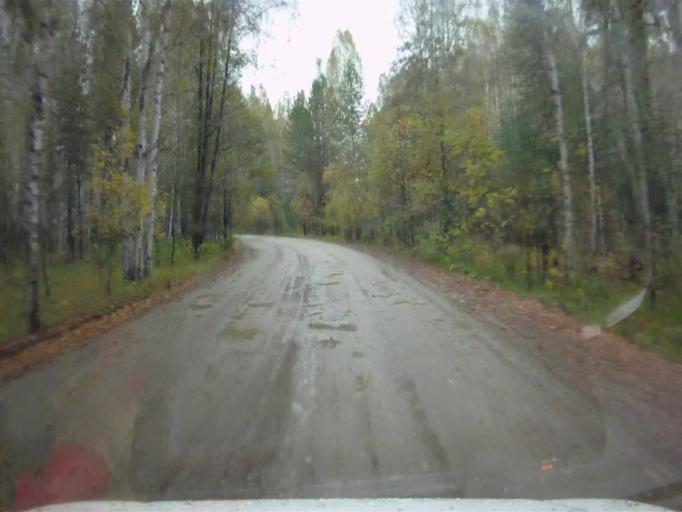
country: RU
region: Chelyabinsk
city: Kyshtym
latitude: 55.8407
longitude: 60.4867
